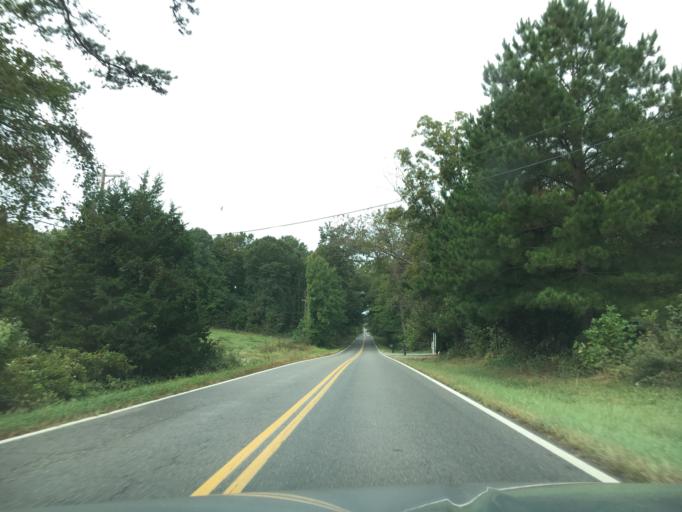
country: US
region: Virginia
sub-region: Goochland County
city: Goochland
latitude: 37.7612
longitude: -77.8755
